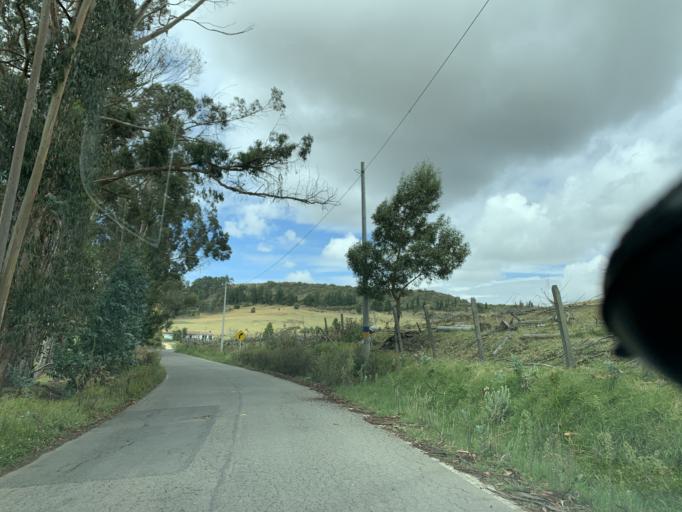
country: CO
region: Boyaca
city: Toca
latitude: 5.5719
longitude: -73.2247
